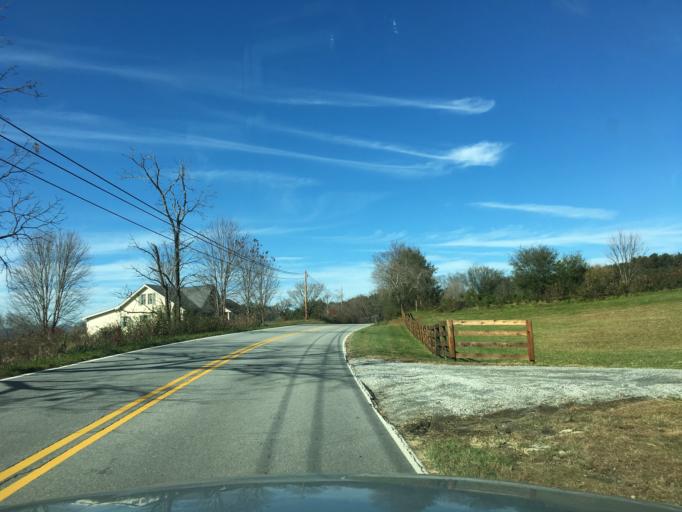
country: US
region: North Carolina
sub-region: Henderson County
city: Etowah
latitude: 35.2392
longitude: -82.6291
